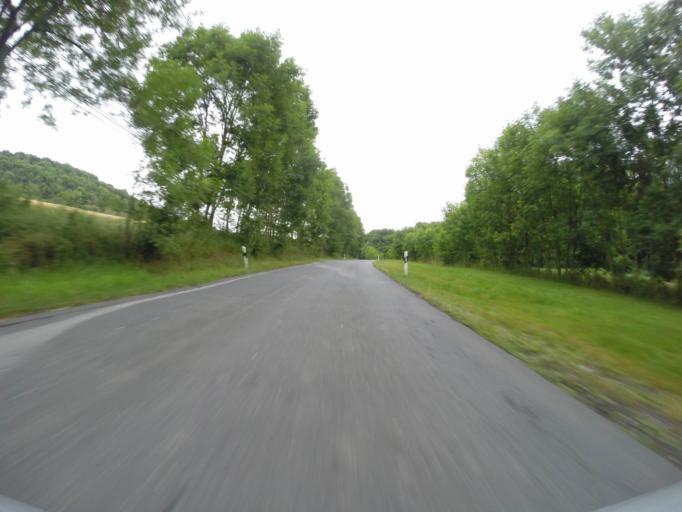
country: DE
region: Thuringia
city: Grosslobichau
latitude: 50.9335
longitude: 11.6850
